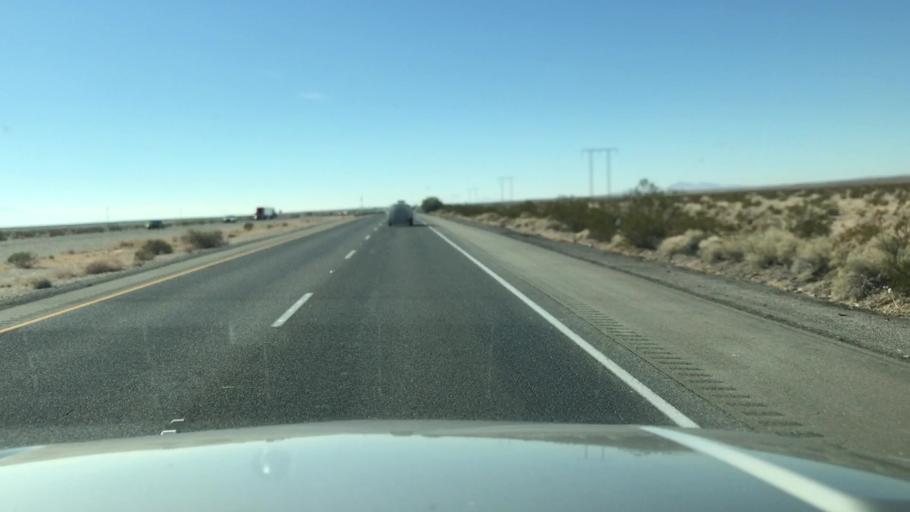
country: US
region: California
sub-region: San Bernardino County
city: Fort Irwin
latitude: 35.0262
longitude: -116.4896
